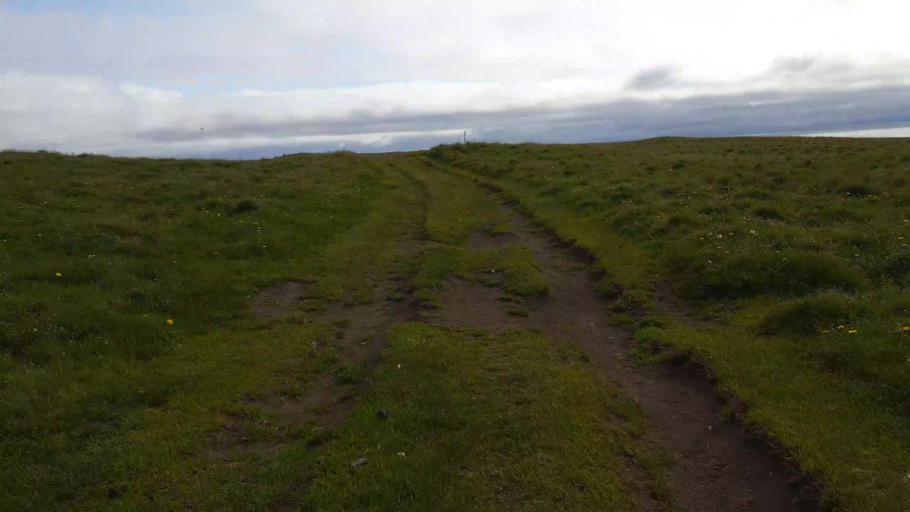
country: IS
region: Northeast
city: Dalvik
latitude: 66.5541
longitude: -18.0000
